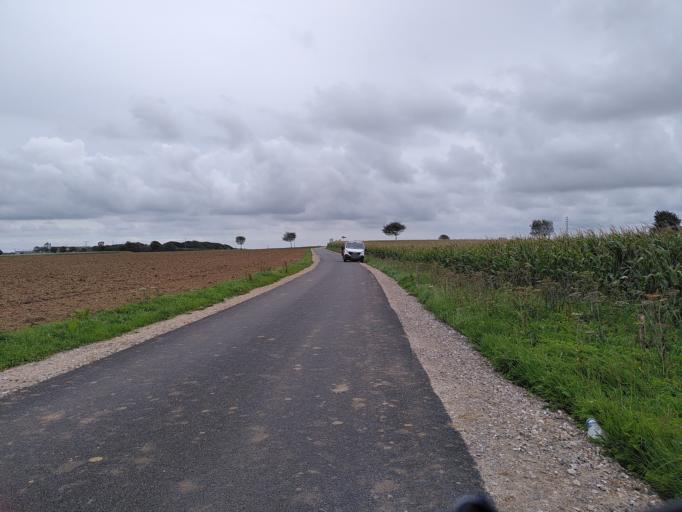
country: FR
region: Nord-Pas-de-Calais
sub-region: Departement du Pas-de-Calais
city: Desvres
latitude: 50.6448
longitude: 1.9637
